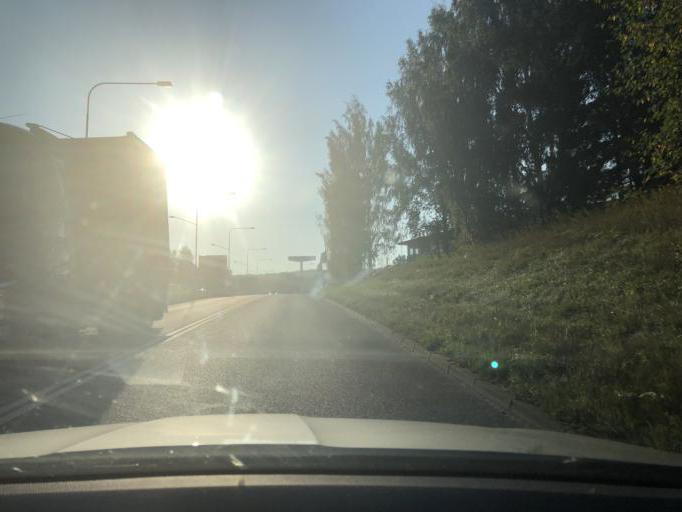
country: SE
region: Joenkoeping
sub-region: Jonkopings Kommun
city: Jonkoping
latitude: 57.7649
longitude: 14.1823
